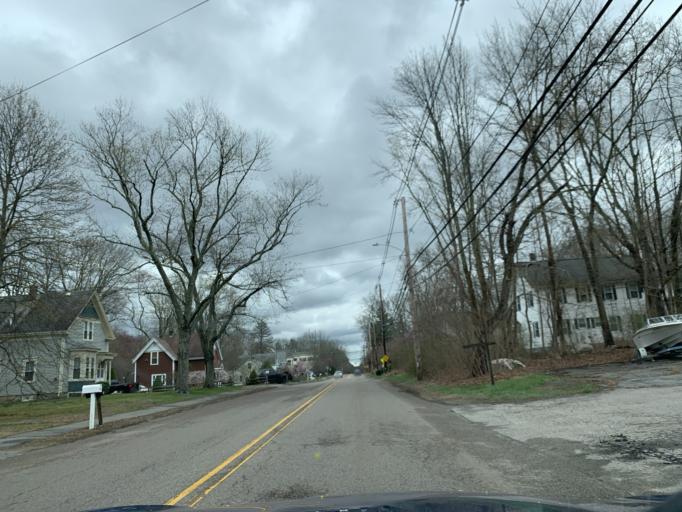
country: US
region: Massachusetts
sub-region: Bristol County
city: Norton
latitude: 41.9477
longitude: -71.2238
